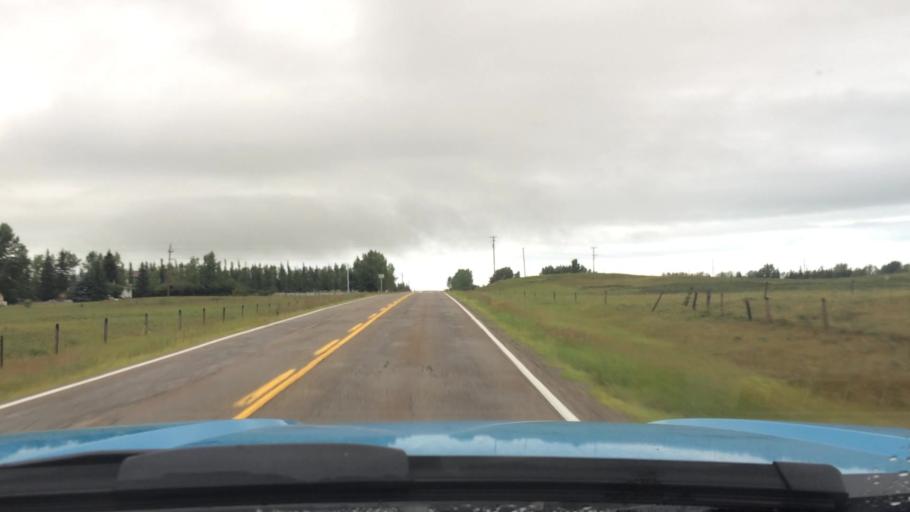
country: CA
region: Alberta
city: Airdrie
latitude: 51.1956
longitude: -114.1412
